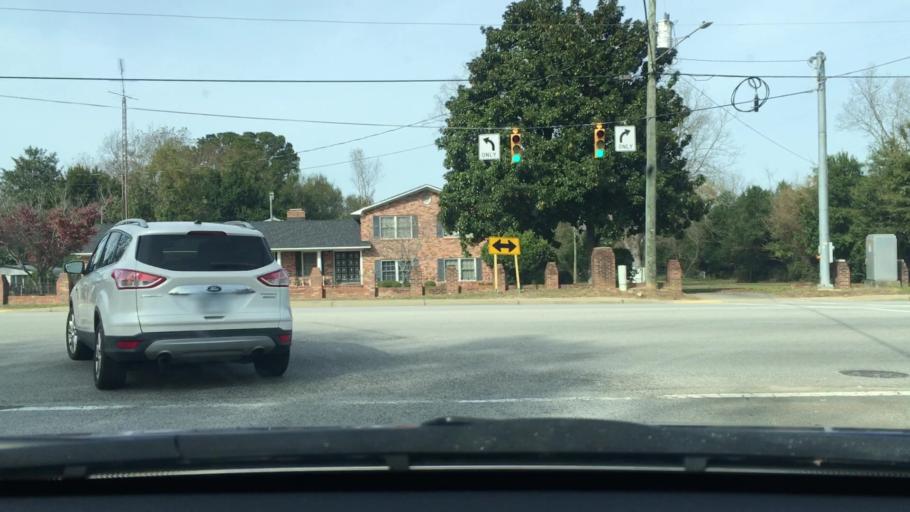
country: US
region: South Carolina
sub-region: Sumter County
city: South Sumter
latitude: 33.9064
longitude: -80.3712
